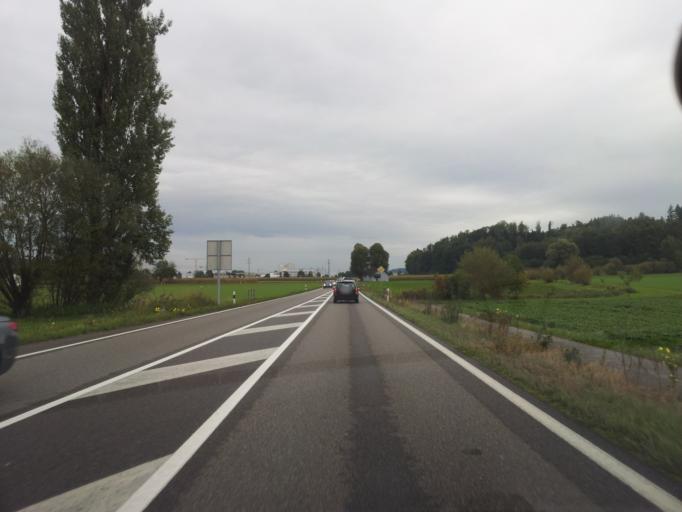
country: CH
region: Aargau
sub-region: Bezirk Lenzburg
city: Othmarsingen
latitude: 47.3812
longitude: 8.2156
